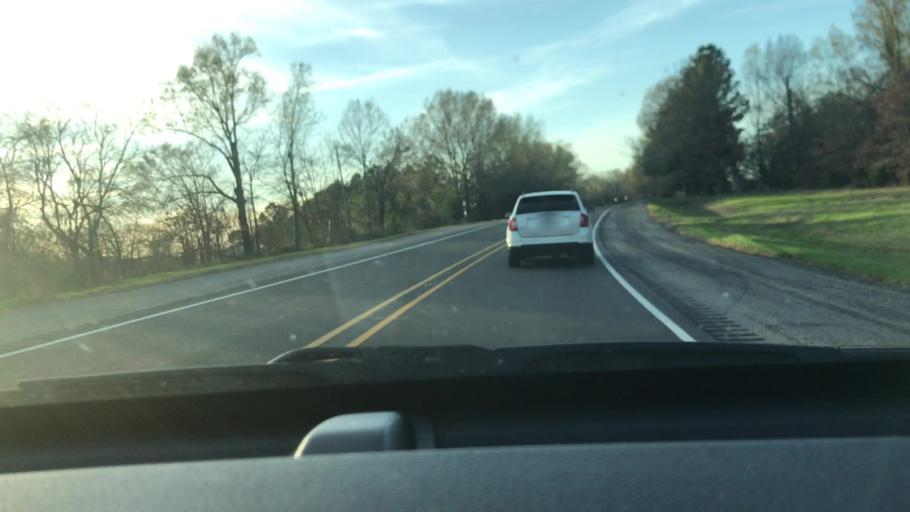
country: US
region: Texas
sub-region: Red River County
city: Clarksville
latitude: 33.5872
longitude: -94.9398
